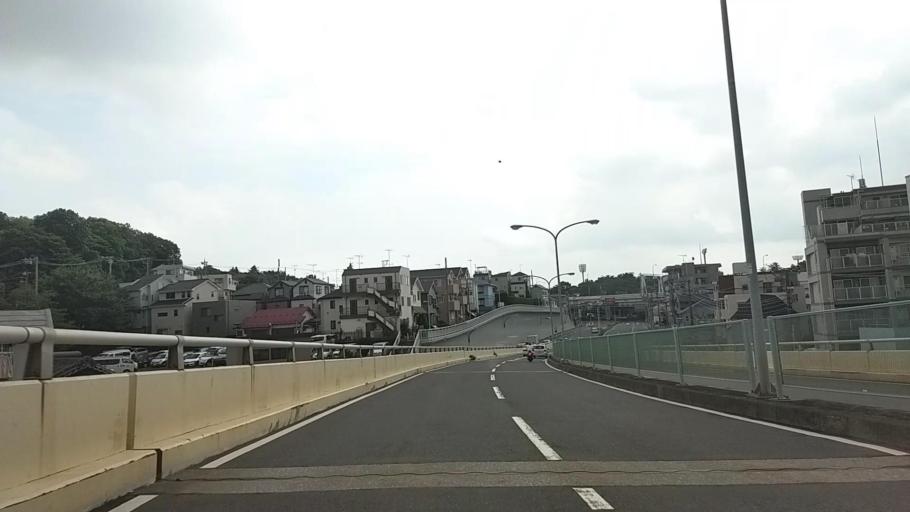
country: JP
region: Kanagawa
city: Yokohama
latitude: 35.4755
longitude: 139.6025
